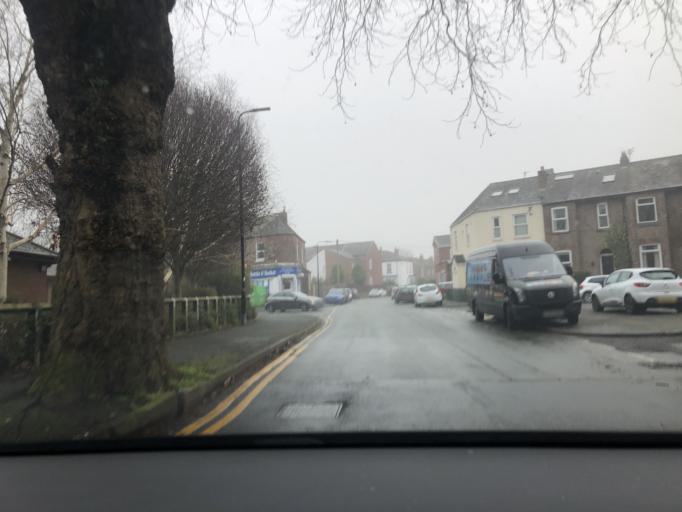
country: GB
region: England
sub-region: Trafford
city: Urmston
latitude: 53.4516
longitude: -2.3654
